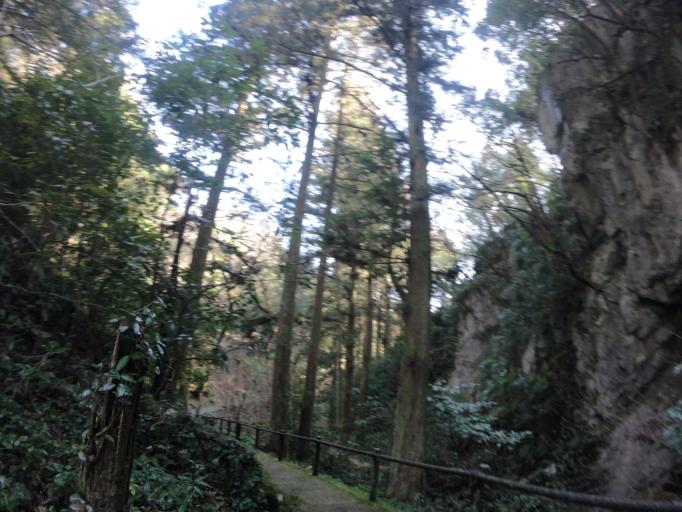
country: JP
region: Yamaguchi
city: Hagi
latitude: 34.2770
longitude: 131.3190
